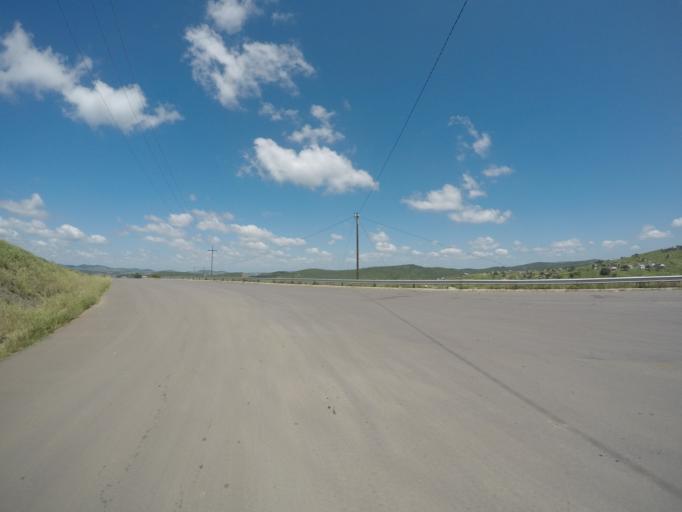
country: ZA
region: KwaZulu-Natal
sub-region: uThungulu District Municipality
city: Empangeni
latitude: -28.6108
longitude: 31.7472
